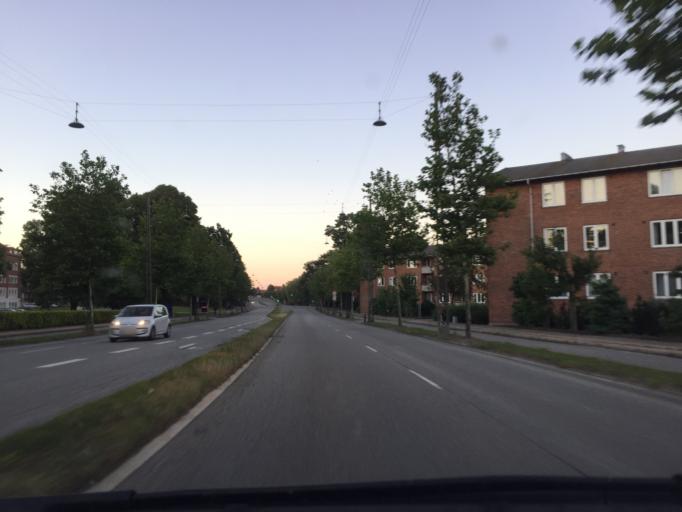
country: DK
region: Capital Region
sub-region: Frederiksberg Kommune
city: Frederiksberg
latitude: 55.7196
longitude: 12.5439
